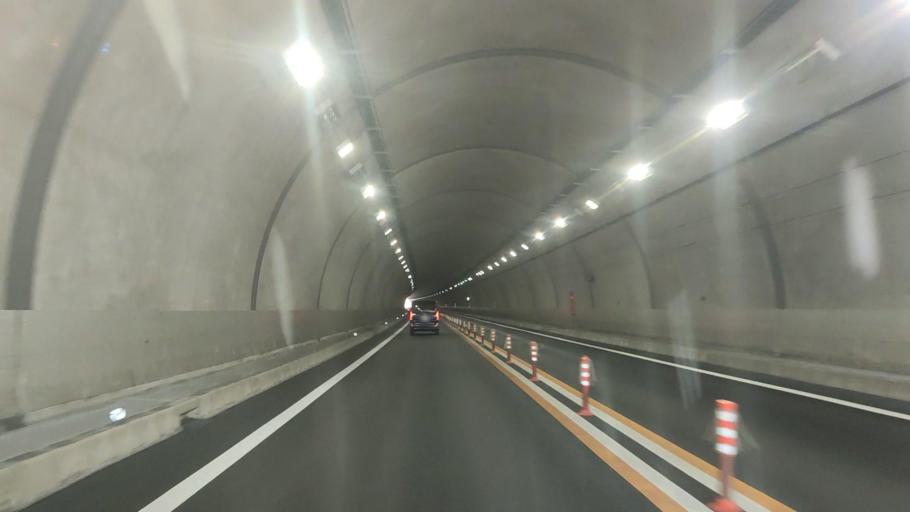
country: JP
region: Fukuoka
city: Nakatsu
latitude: 33.5151
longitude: 131.2765
